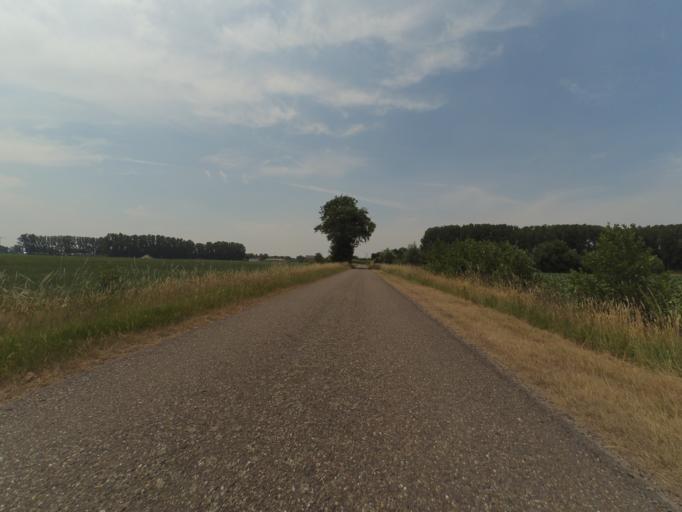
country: BE
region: Flanders
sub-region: Provincie Antwerpen
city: Brecht
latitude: 51.4005
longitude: 4.6595
